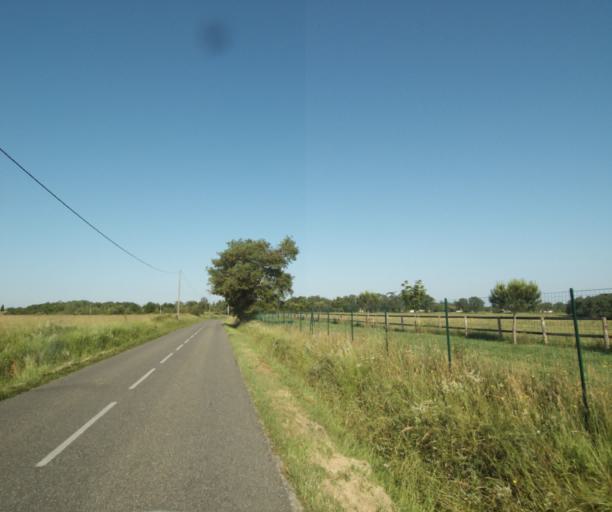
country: FR
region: Midi-Pyrenees
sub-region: Departement du Tarn-et-Garonne
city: Montauban
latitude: 44.0154
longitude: 1.4012
